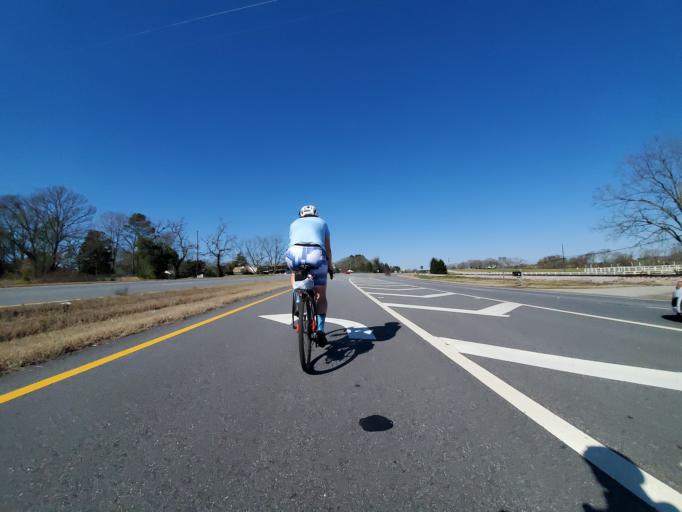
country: US
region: Georgia
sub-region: Clarke County
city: Country Club Estates
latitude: 34.0051
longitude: -83.4574
